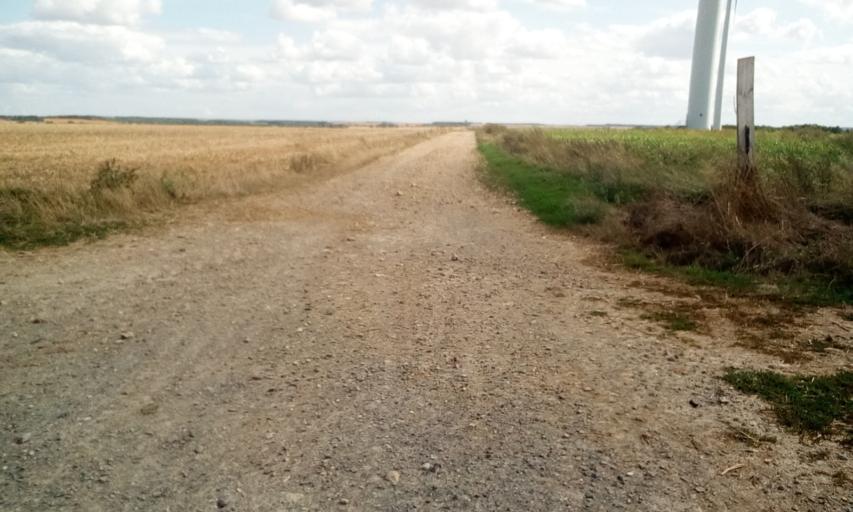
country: FR
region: Lower Normandy
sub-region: Departement du Calvados
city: Bellengreville
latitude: 49.0965
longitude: -0.2261
